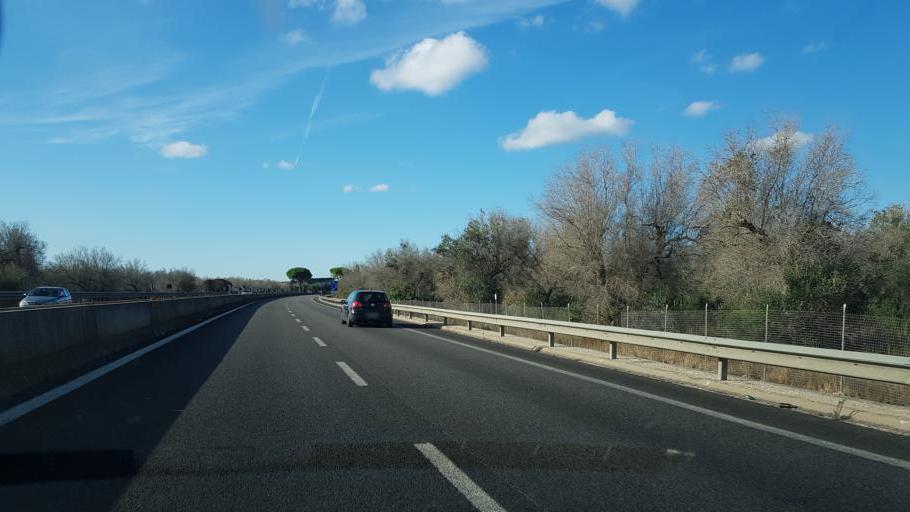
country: IT
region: Apulia
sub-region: Provincia di Lecce
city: Squinzano
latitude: 40.4520
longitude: 18.0672
